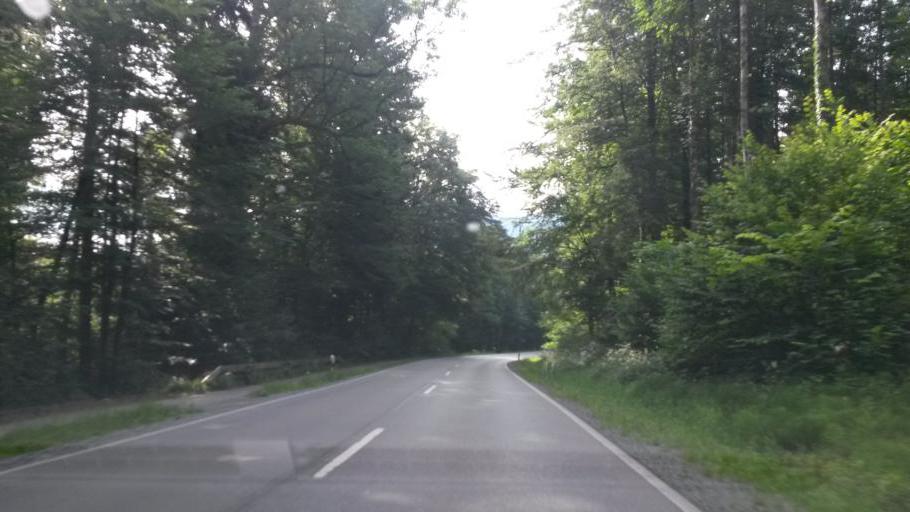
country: DE
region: Bavaria
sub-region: Upper Bavaria
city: Aschau im Chiemgau
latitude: 47.7929
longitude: 12.3064
